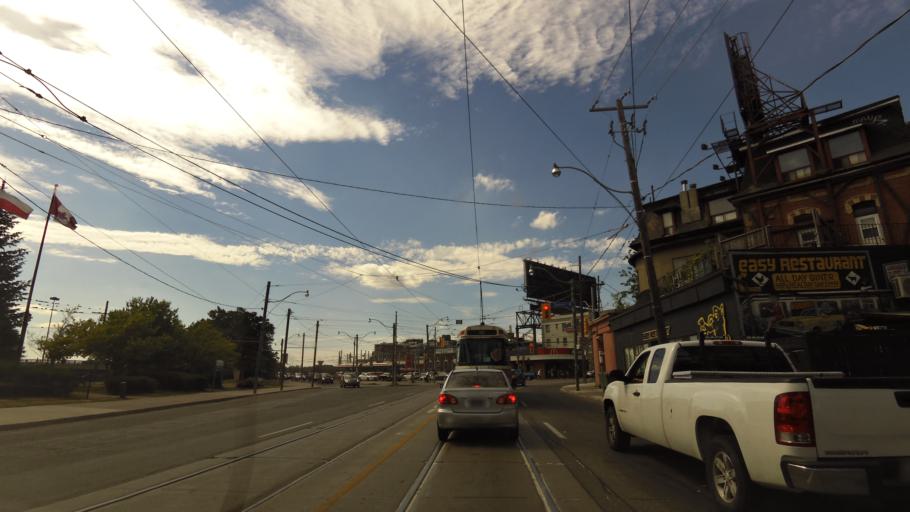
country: CA
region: Ontario
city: Toronto
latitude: 43.6384
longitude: -79.4455
